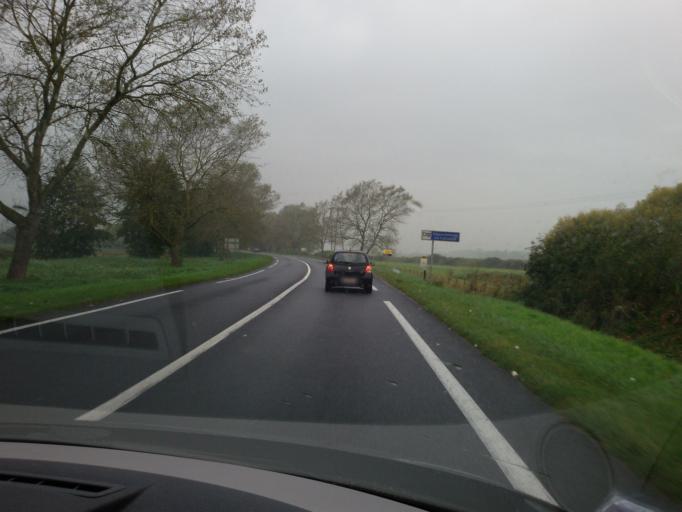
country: FR
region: Lower Normandy
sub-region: Departement du Calvados
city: Ablon
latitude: 49.4118
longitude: 0.2974
